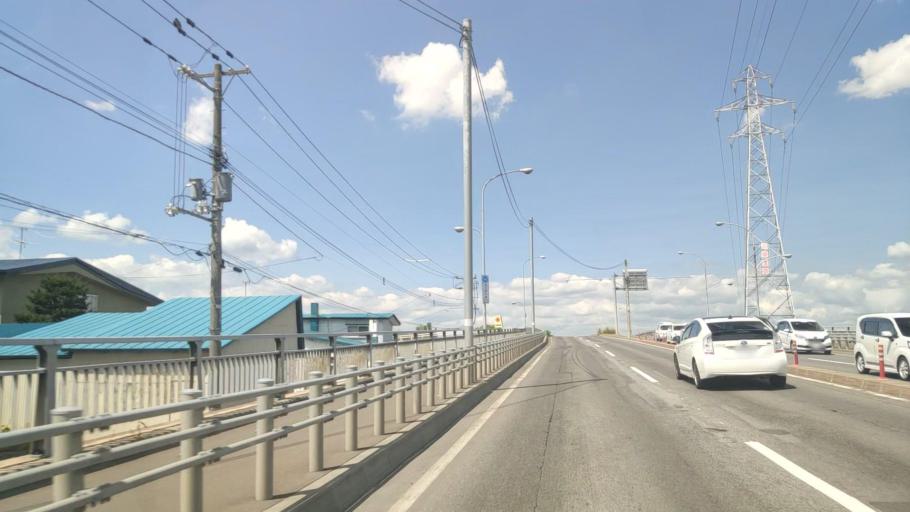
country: JP
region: Hokkaido
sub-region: Asahikawa-shi
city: Asahikawa
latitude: 43.7958
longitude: 142.3984
